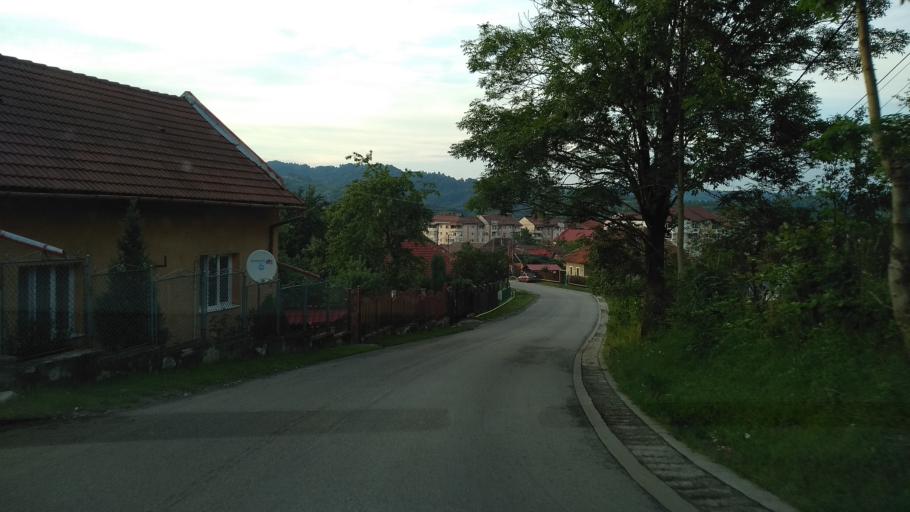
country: RO
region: Hunedoara
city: Vulcan
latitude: 45.3714
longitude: 23.2815
